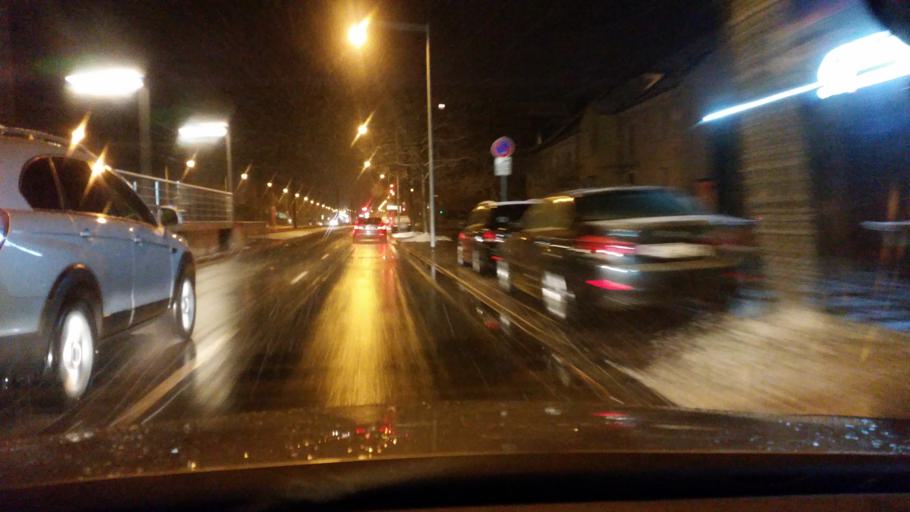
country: DE
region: Lower Saxony
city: Hannover
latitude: 52.3643
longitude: 9.7733
